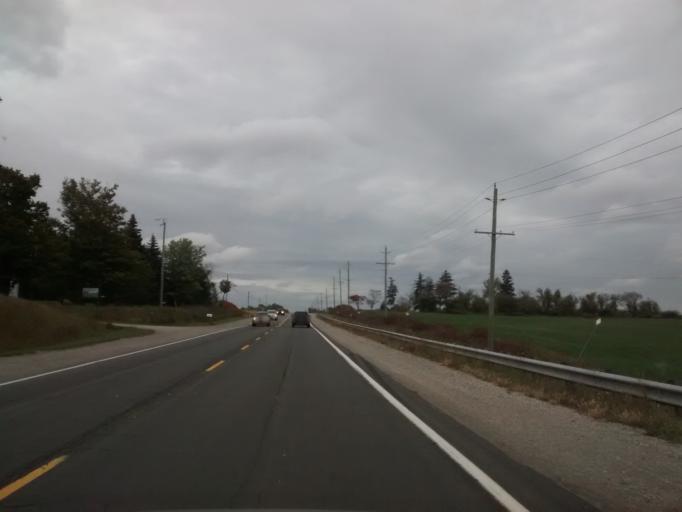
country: CA
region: Ontario
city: Ancaster
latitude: 43.0190
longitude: -80.0006
